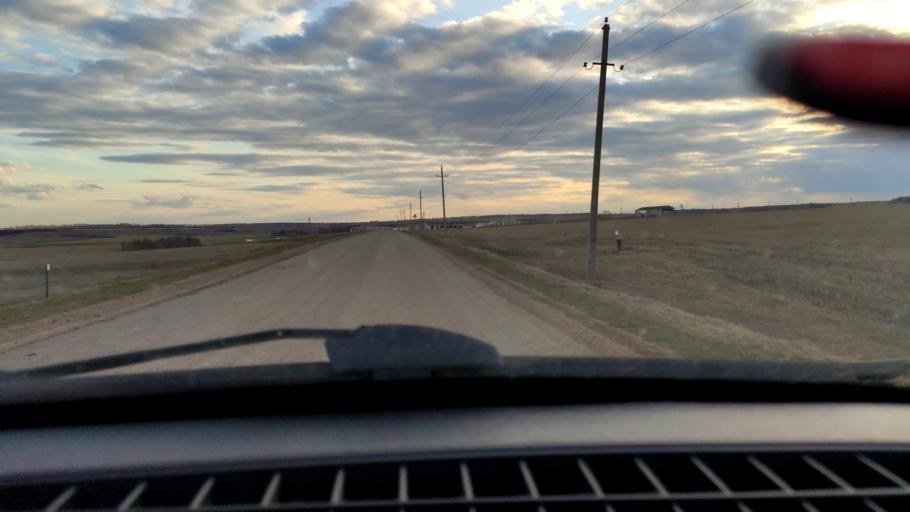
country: RU
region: Bashkortostan
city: Tolbazy
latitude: 53.9971
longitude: 55.6761
